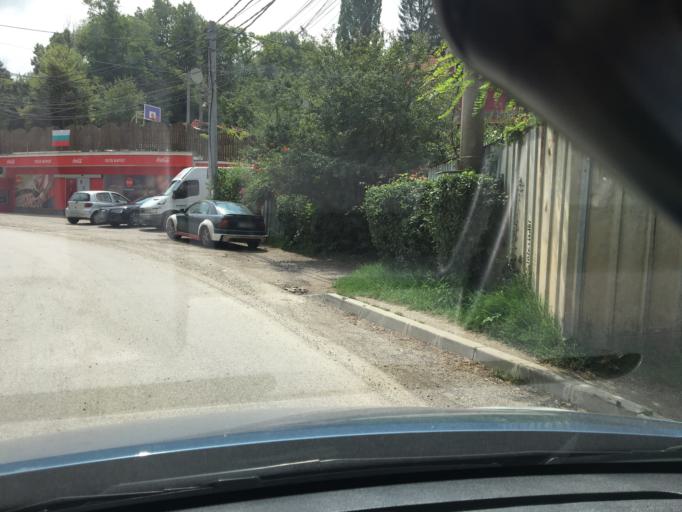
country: BG
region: Sofia-Capital
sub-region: Stolichna Obshtina
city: Sofia
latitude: 42.6105
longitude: 23.3634
